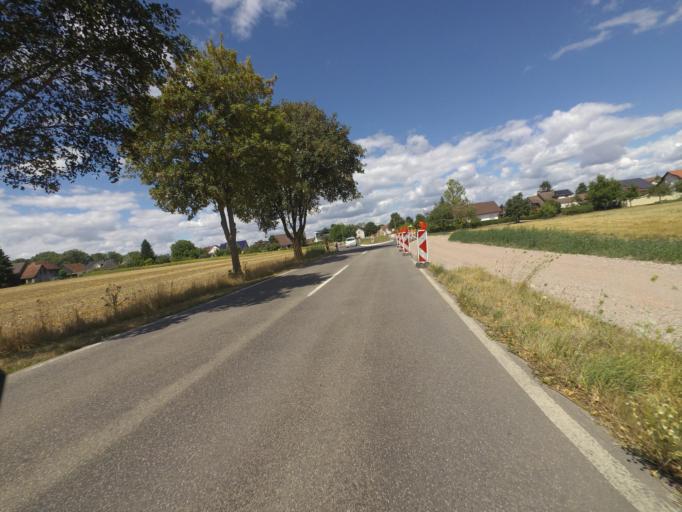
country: DE
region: Baden-Wuerttemberg
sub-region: Karlsruhe Region
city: Ottenhofen
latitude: 48.7490
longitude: 8.0985
